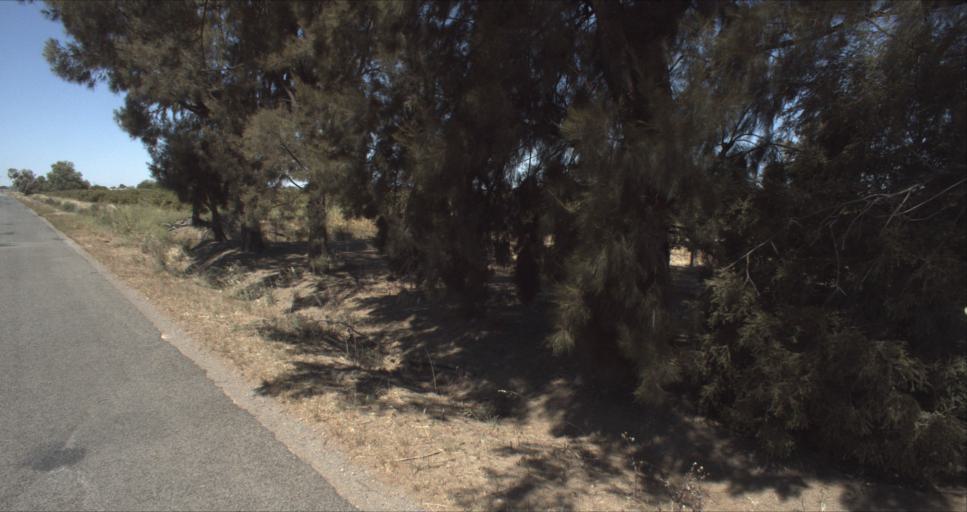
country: AU
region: New South Wales
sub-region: Leeton
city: Leeton
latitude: -34.5324
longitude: 146.3915
